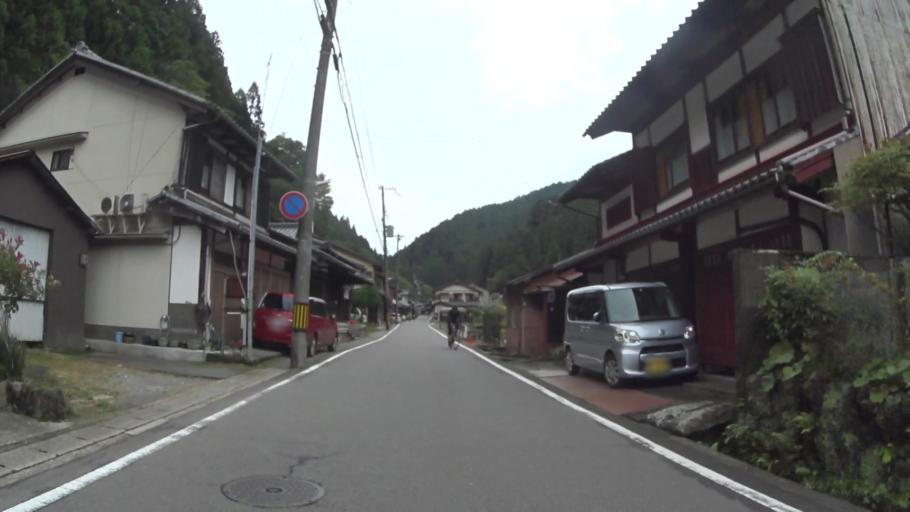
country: JP
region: Kyoto
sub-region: Kyoto-shi
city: Kamigyo-ku
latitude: 35.1154
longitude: 135.7744
